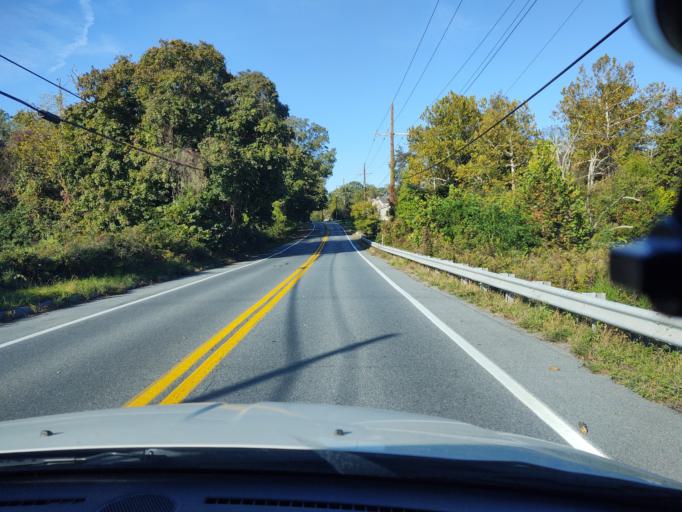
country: US
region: Maryland
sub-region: Prince George's County
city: Glenn Dale
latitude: 39.0069
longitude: -76.7679
